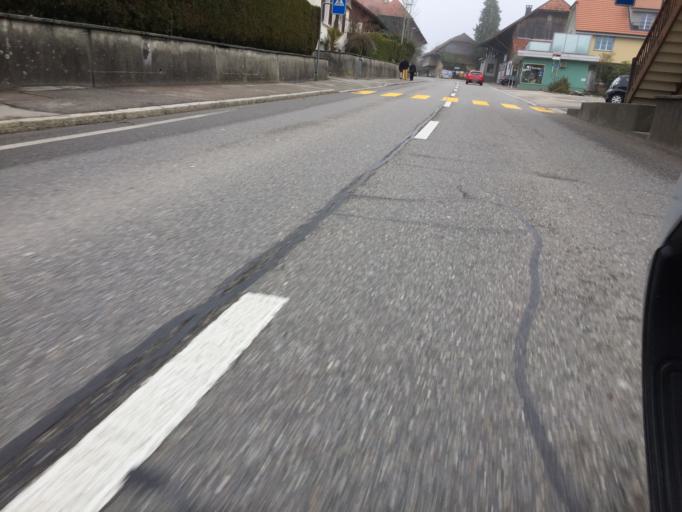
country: CH
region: Bern
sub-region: Seeland District
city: Schupfen
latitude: 47.0625
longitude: 7.4110
